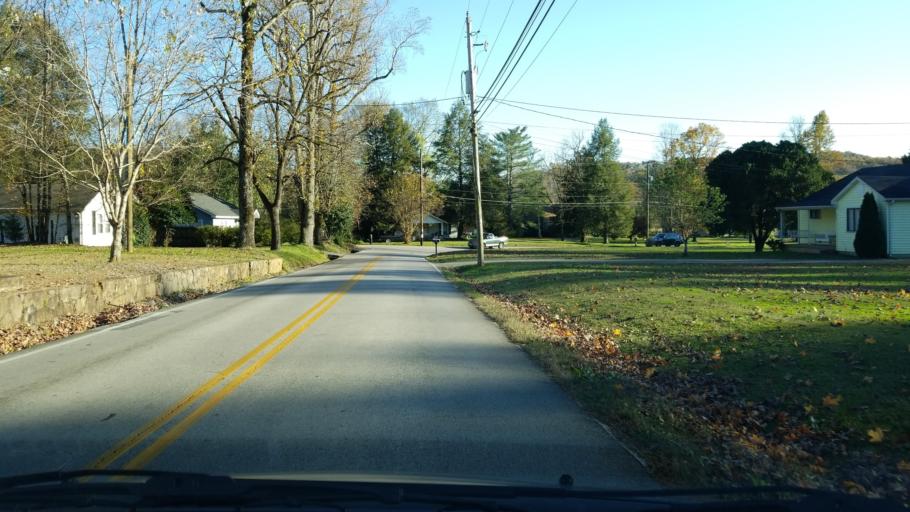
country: US
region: Tennessee
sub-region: Hamilton County
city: Falling Water
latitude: 35.2035
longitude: -85.2541
